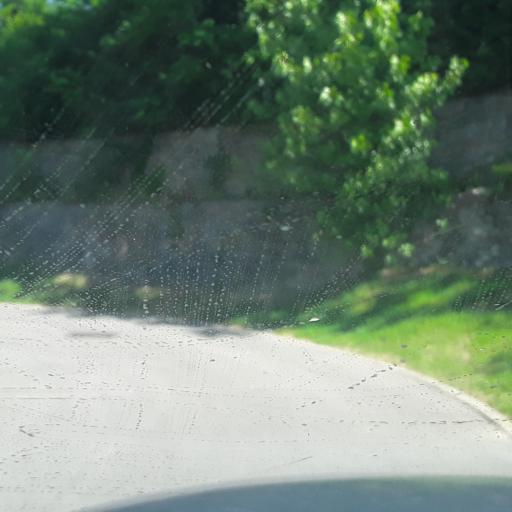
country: US
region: Tennessee
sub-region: Williamson County
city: Brentwood Estates
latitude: 36.0321
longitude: -86.6983
